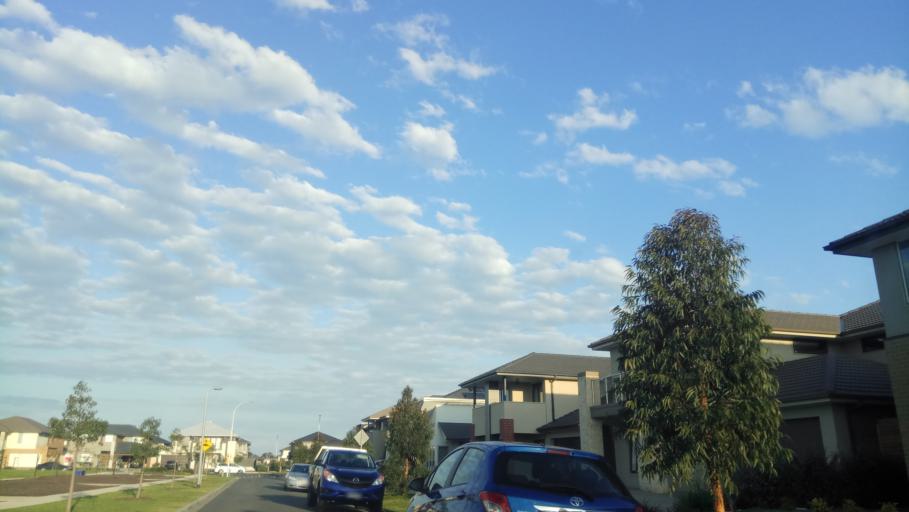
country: AU
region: Victoria
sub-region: Wyndham
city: Point Cook
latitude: -37.9032
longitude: 144.7583
